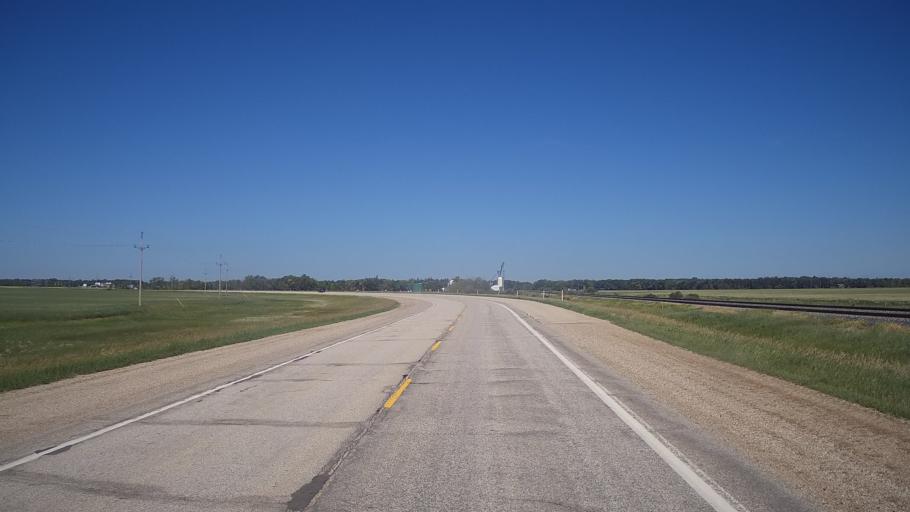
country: CA
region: Manitoba
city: Portage la Prairie
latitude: 50.1240
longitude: -98.5679
